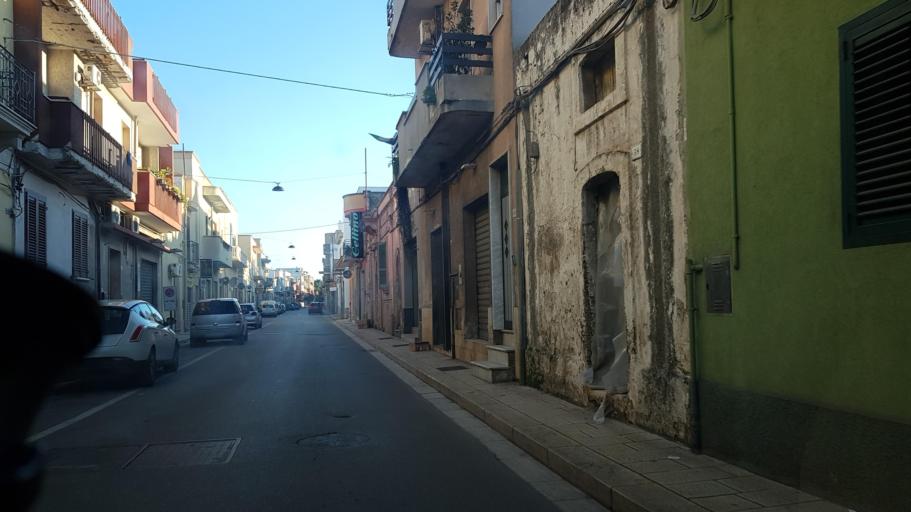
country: IT
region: Apulia
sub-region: Provincia di Brindisi
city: Latiano
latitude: 40.5509
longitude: 17.7176
